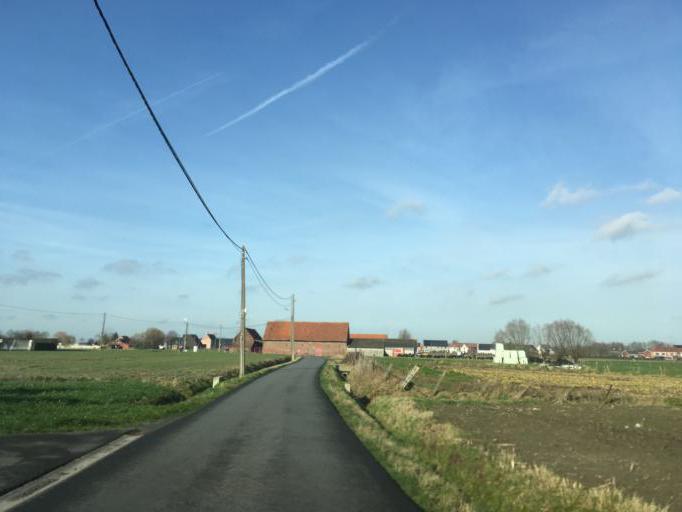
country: BE
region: Flanders
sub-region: Provincie West-Vlaanderen
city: Ardooie
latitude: 50.9527
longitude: 3.1667
